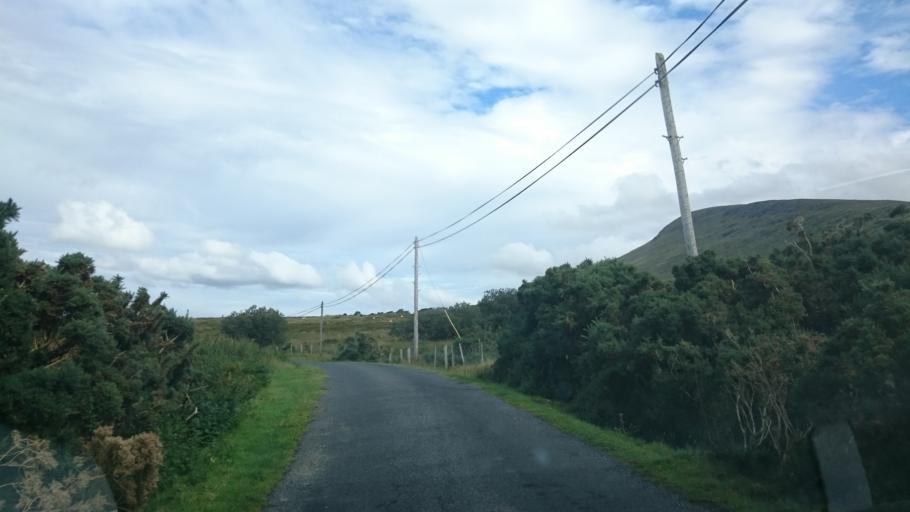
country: IE
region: Connaught
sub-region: Maigh Eo
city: Westport
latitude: 53.9332
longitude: -9.5627
